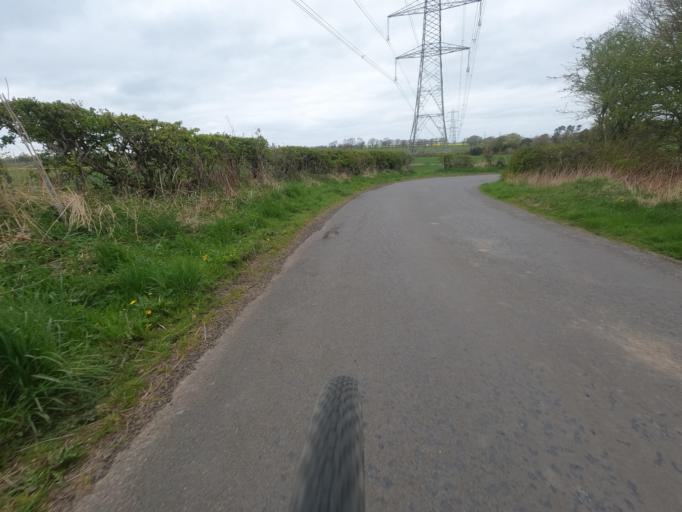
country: GB
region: England
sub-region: Northumberland
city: Meldon
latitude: 55.0651
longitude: -1.8387
